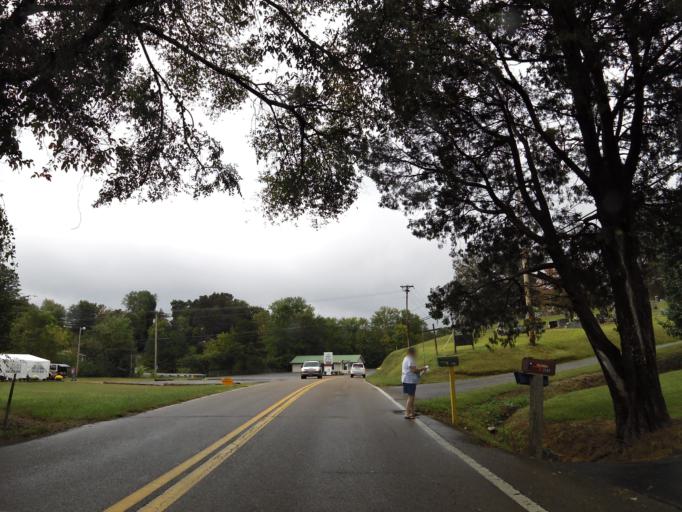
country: US
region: Tennessee
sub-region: Bradley County
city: Cleveland
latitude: 35.1880
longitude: -84.9380
